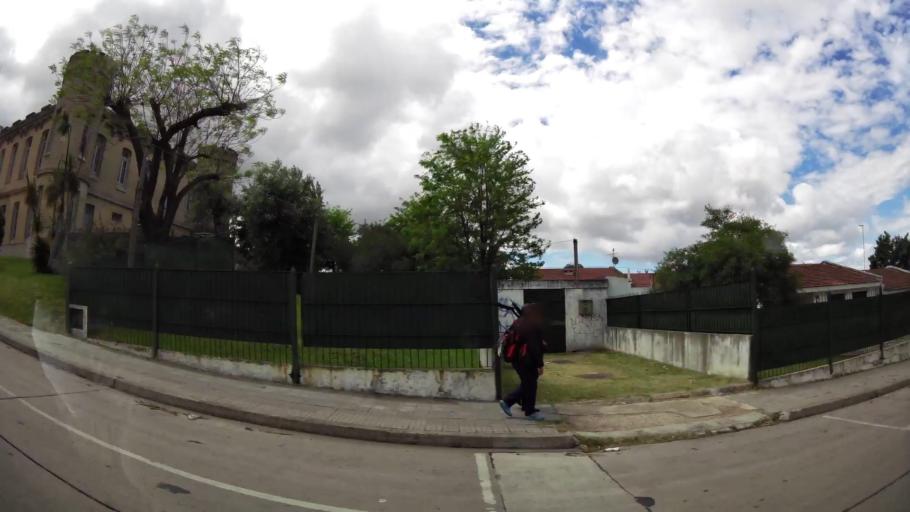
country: UY
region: Montevideo
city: Montevideo
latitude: -34.8579
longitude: -56.1647
